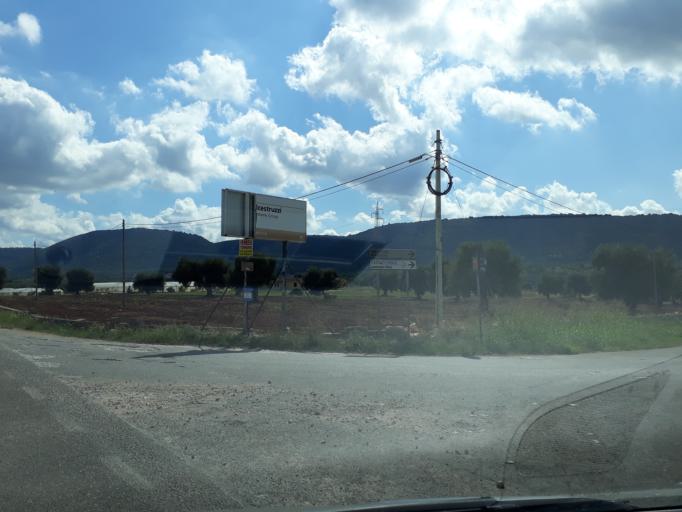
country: IT
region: Apulia
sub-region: Provincia di Brindisi
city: Pezze di Greco
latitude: 40.8044
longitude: 17.3936
